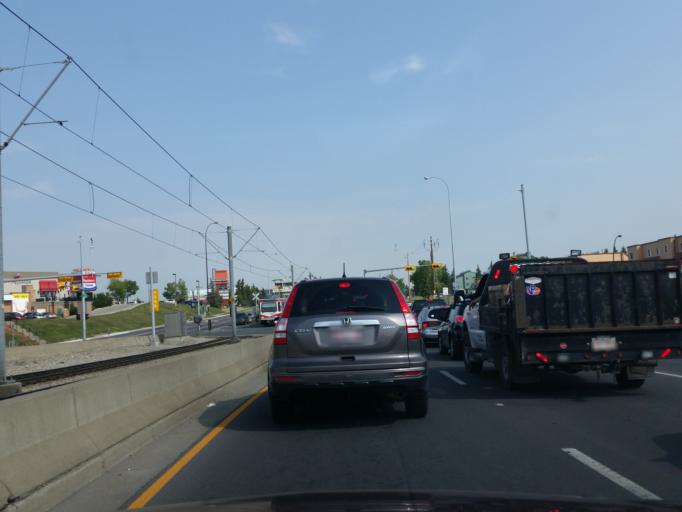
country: CA
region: Alberta
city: Calgary
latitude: 51.0707
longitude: -113.9816
